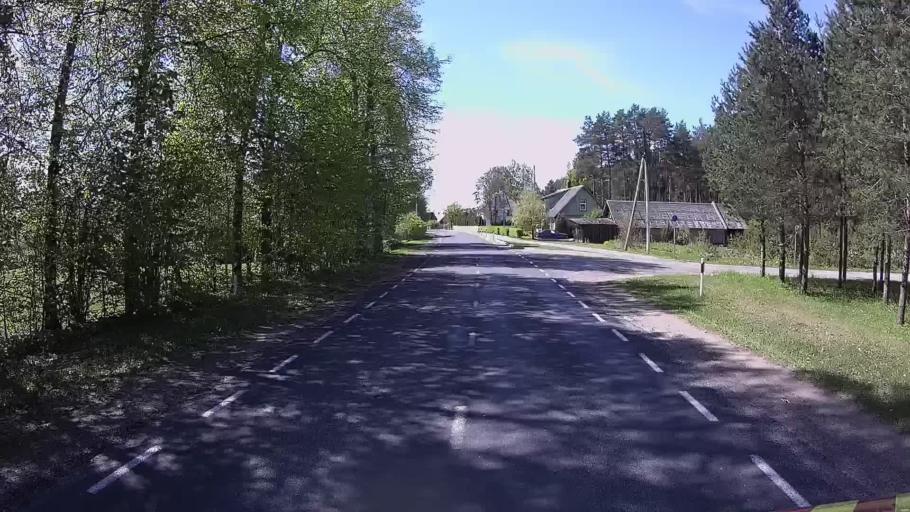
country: EE
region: Polvamaa
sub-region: Raepina vald
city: Rapina
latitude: 58.0105
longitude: 27.3542
